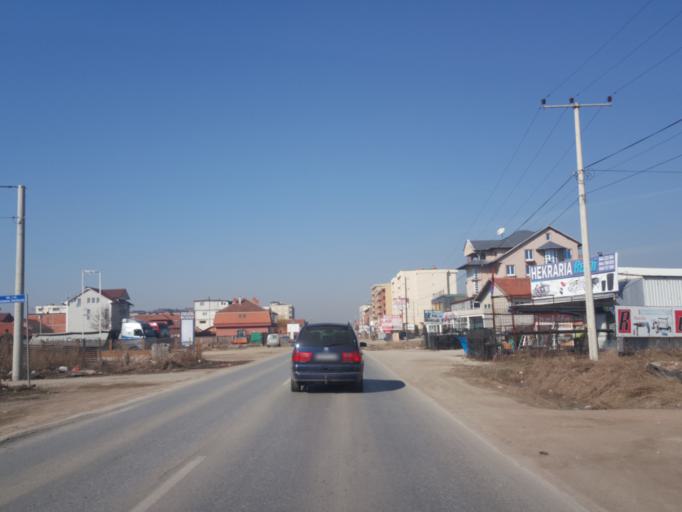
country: XK
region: Mitrovica
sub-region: Vushtrri
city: Vushtrri
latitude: 42.8246
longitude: 20.9740
